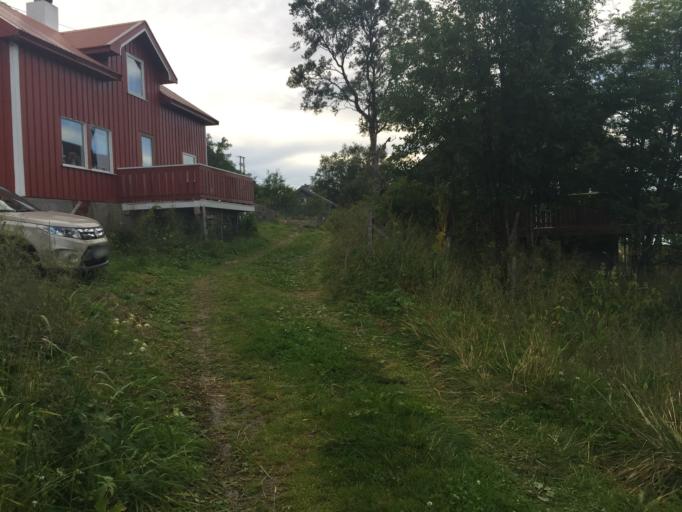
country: NO
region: Nordland
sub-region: Vagan
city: Kabelvag
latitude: 68.3270
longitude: 14.3975
